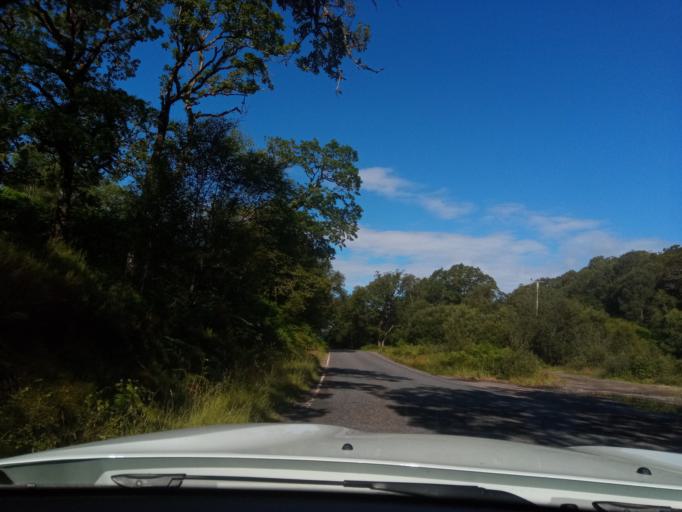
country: GB
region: Scotland
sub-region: Argyll and Bute
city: Isle Of Mull
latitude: 56.6979
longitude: -5.6869
